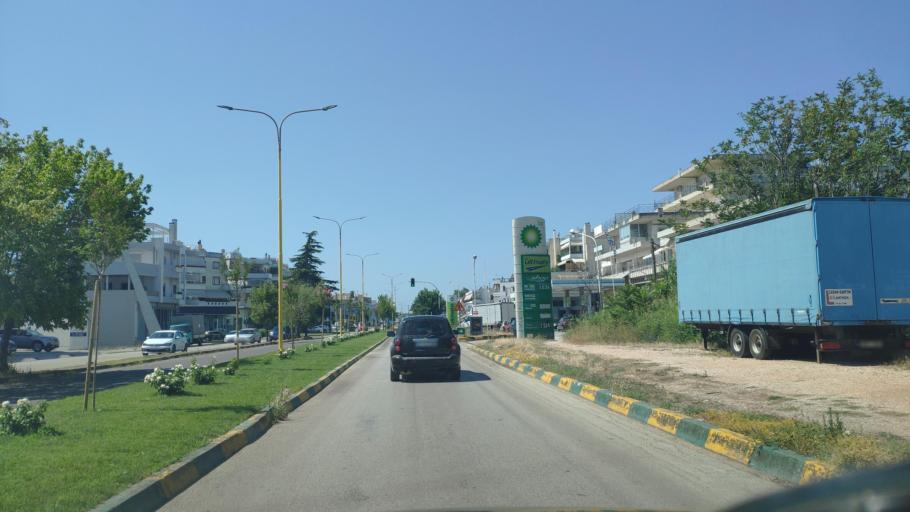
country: GR
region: Epirus
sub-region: Nomos Artas
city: Arta
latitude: 39.1562
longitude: 20.9789
